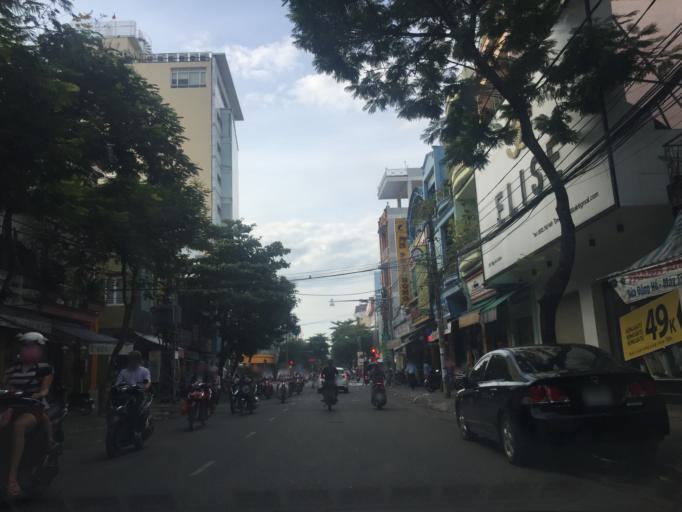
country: VN
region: Da Nang
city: Da Nang
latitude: 16.0710
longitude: 108.2133
